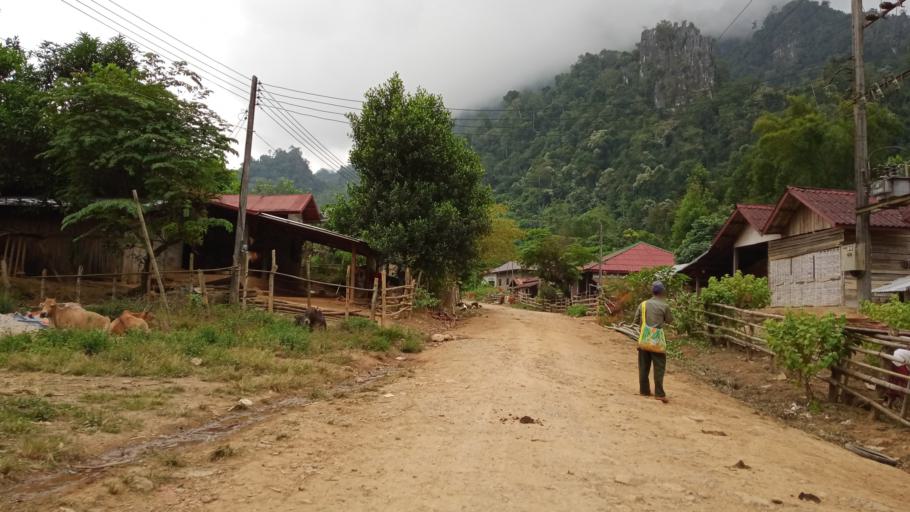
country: LA
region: Xiangkhoang
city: Phonsavan
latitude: 19.0835
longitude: 103.0121
